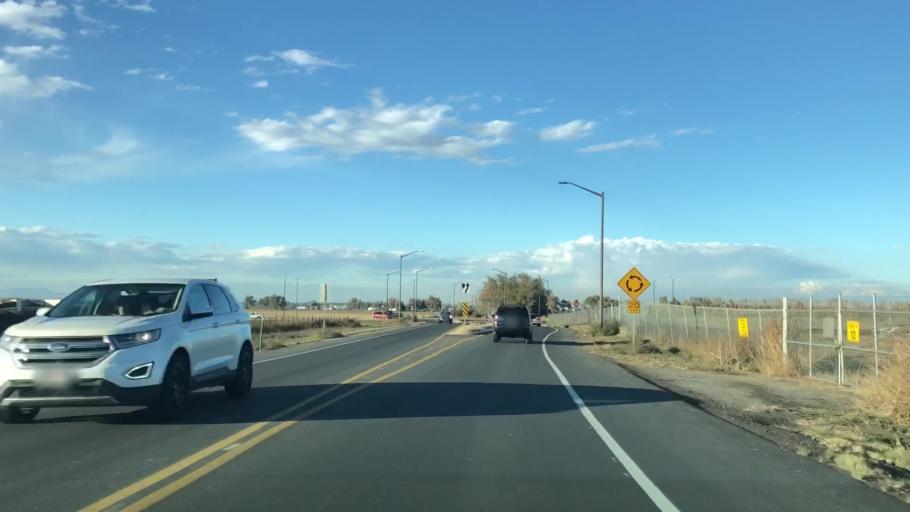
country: US
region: Colorado
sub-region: Larimer County
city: Loveland
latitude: 40.4640
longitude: -105.0203
